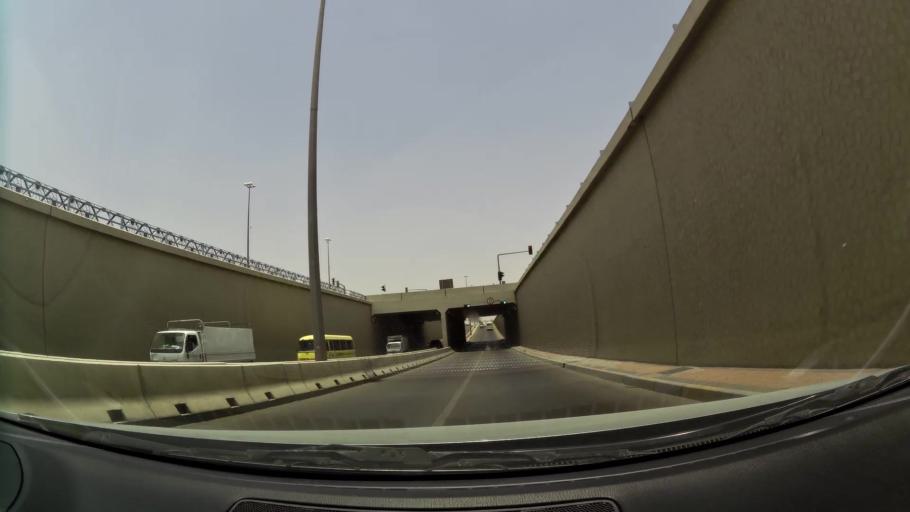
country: AE
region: Abu Dhabi
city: Al Ain
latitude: 24.2056
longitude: 55.7613
